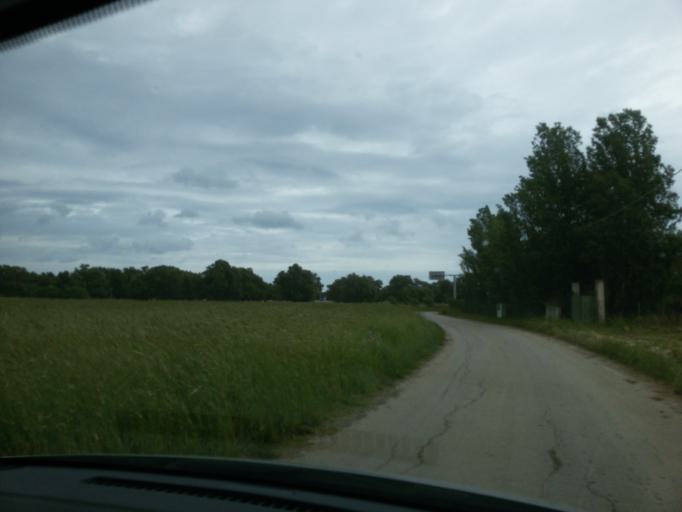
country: IT
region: Apulia
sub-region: Provincia di Brindisi
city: Brindisi
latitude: 40.6575
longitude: 17.9271
